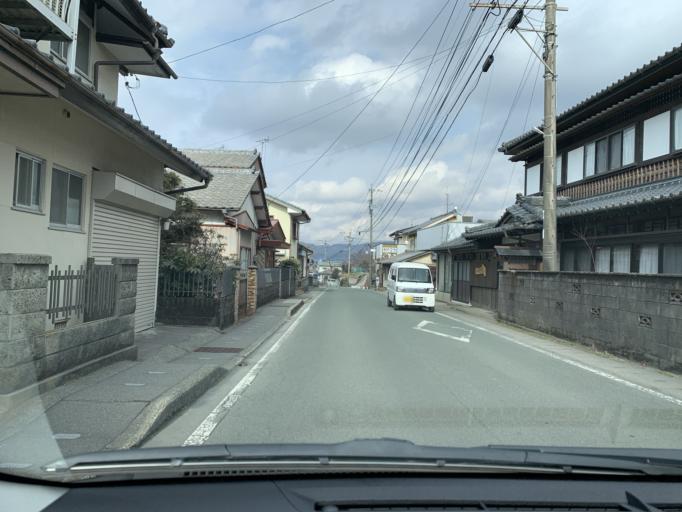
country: JP
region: Kumamoto
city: Aso
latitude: 32.9425
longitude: 131.1159
